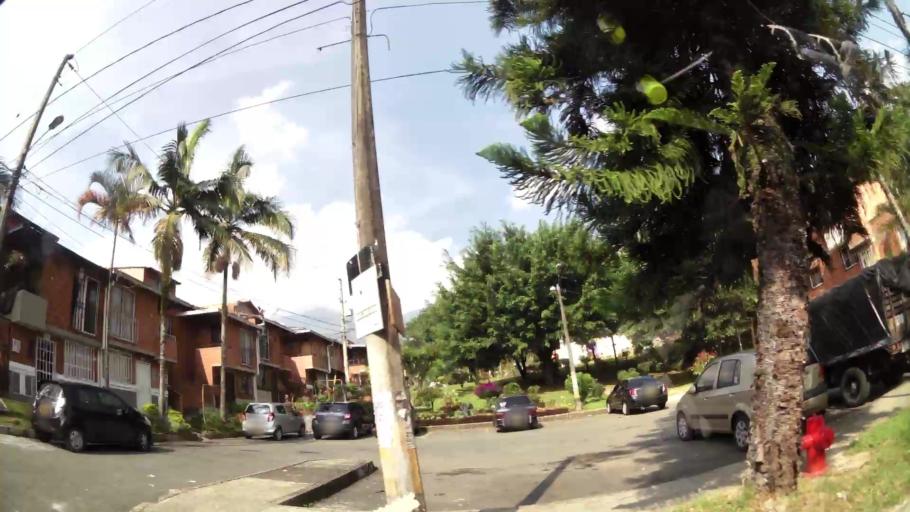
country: CO
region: Antioquia
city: La Estrella
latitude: 6.1672
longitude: -75.6430
